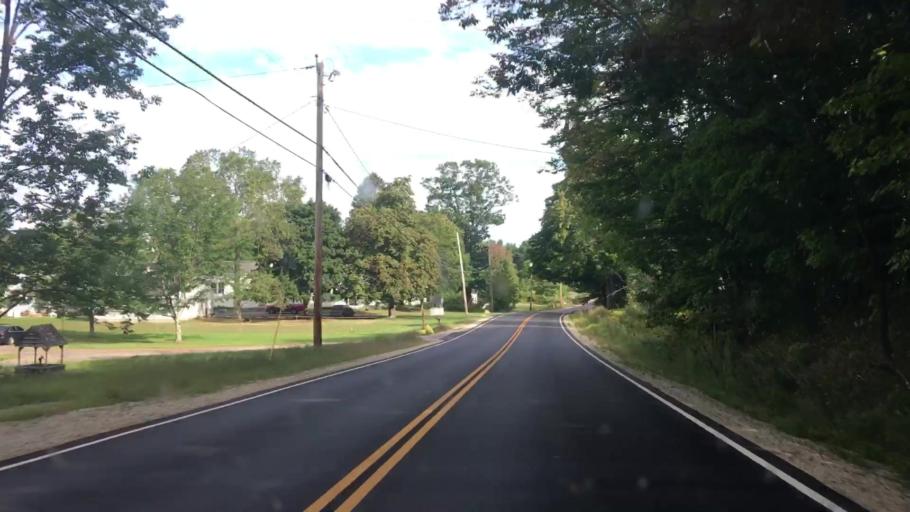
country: US
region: Maine
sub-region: Cumberland County
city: Cumberland Center
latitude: 43.7780
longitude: -70.3029
